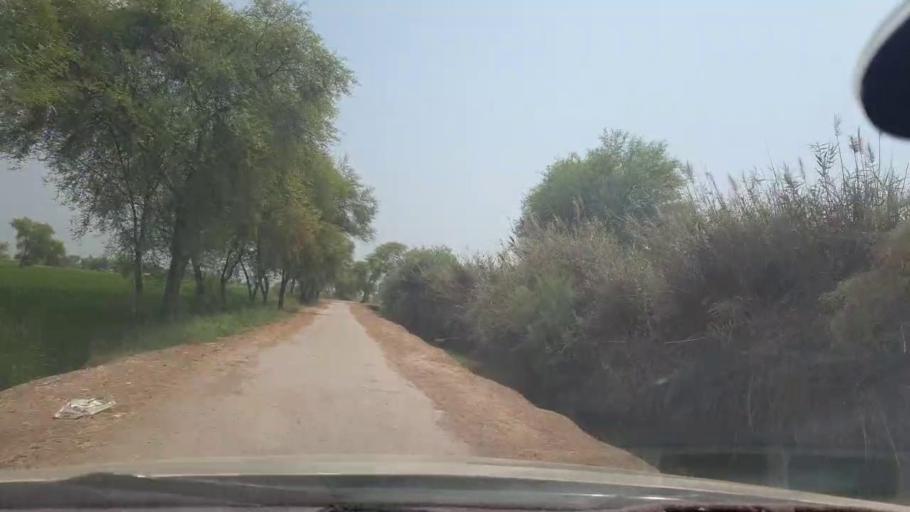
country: PK
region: Sindh
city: Jacobabad
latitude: 28.1771
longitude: 68.3834
